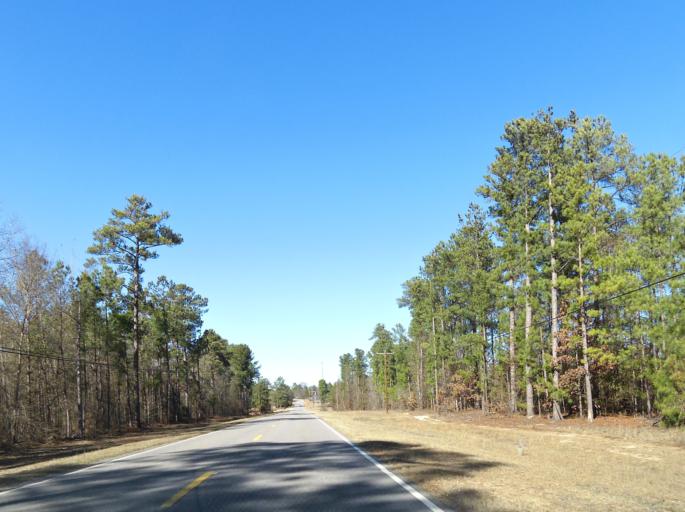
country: US
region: Georgia
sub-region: Bibb County
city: West Point
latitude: 32.7930
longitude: -83.7953
